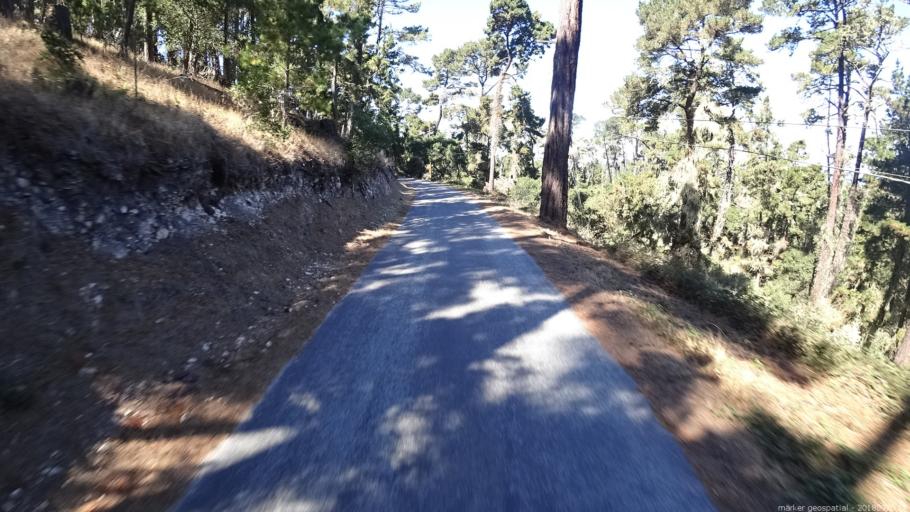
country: US
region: California
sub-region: Monterey County
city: Monterey
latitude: 36.5661
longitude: -121.8856
